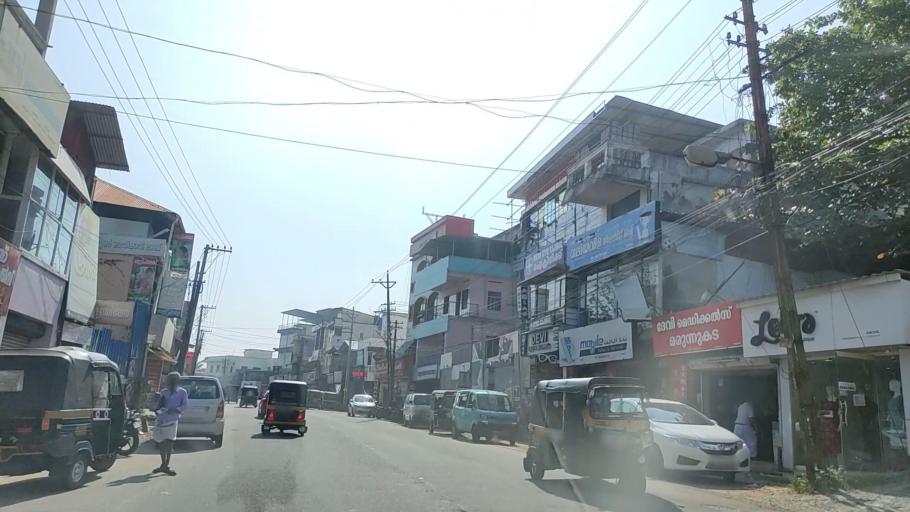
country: IN
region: Kerala
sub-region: Kollam
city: Punalur
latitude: 8.9269
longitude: 76.9153
